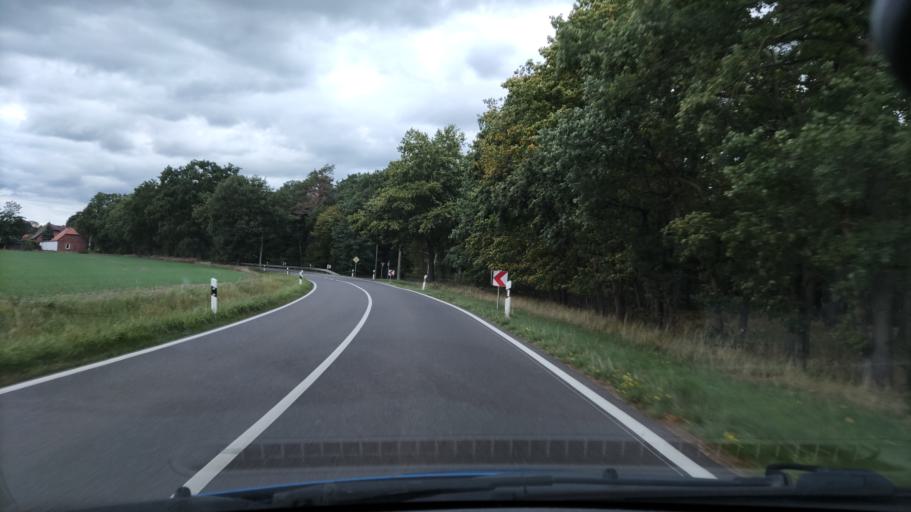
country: DE
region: Mecklenburg-Vorpommern
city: Lubtheen
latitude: 53.3528
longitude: 10.9609
